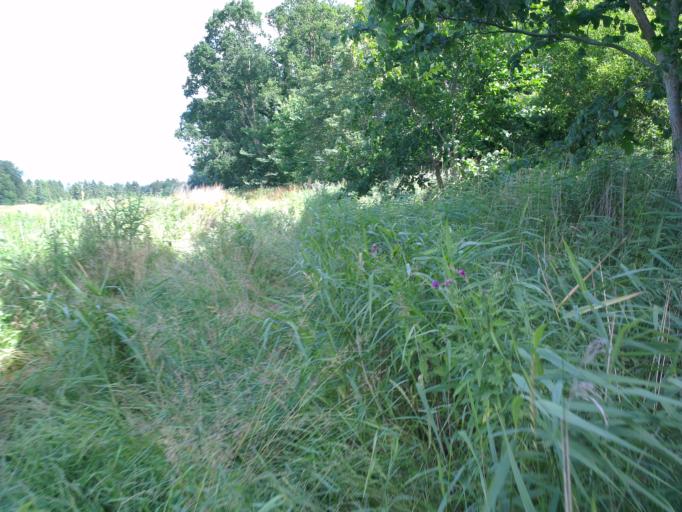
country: DK
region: Capital Region
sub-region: Frederikssund Kommune
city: Jaegerspris
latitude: 55.8896
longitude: 11.9950
